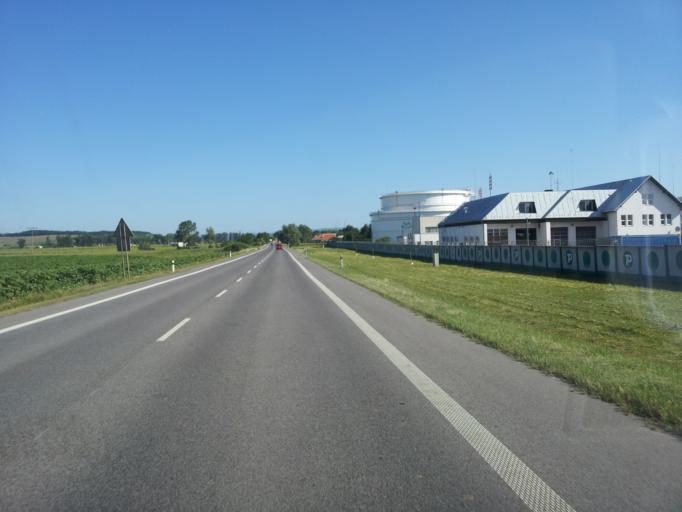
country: SK
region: Nitriansky
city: Sahy
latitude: 48.1002
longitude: 18.8926
